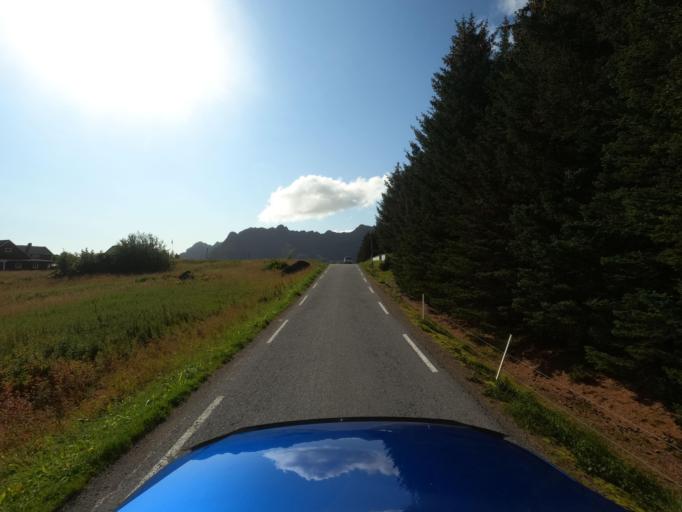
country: NO
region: Nordland
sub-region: Vestvagoy
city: Leknes
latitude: 68.1218
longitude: 13.7404
